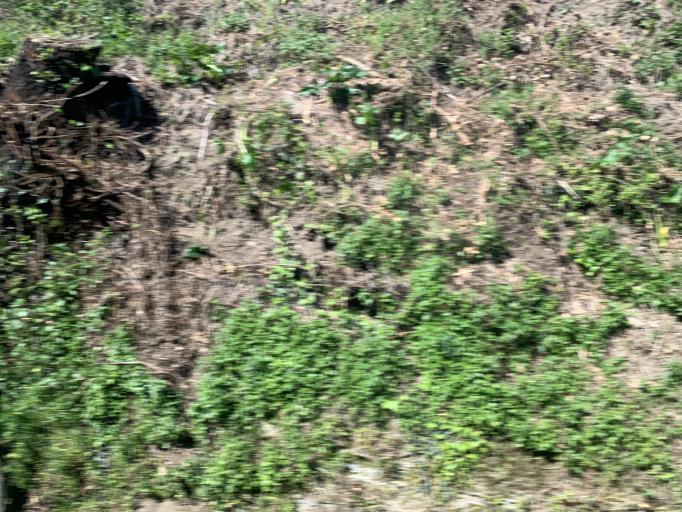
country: IT
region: Latium
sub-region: Citta metropolitana di Roma Capitale
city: Marino
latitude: 41.7811
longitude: 12.6433
